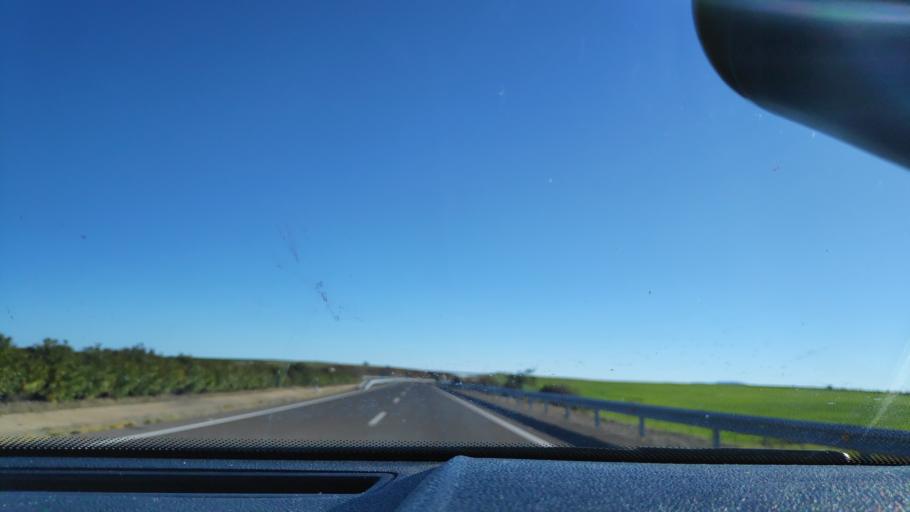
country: ES
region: Extremadura
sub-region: Provincia de Badajoz
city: Fuente de Cantos
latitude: 38.1955
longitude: -6.2829
